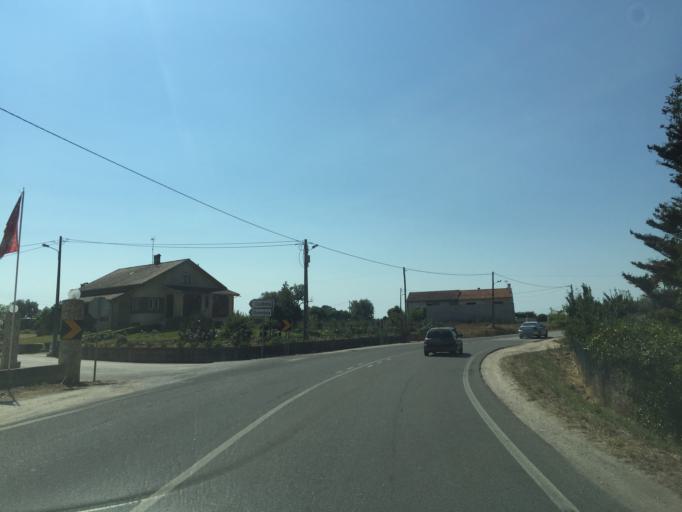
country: PT
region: Coimbra
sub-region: Cantanhede
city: Cantanhede
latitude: 40.3565
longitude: -8.5377
